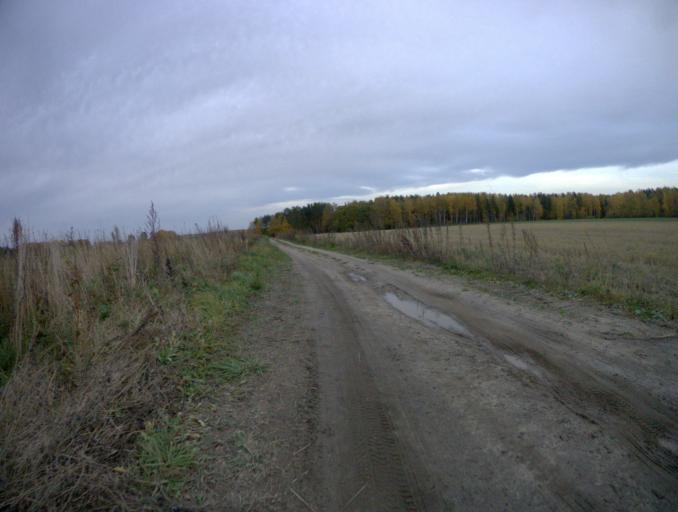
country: RU
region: Vladimir
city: Kommunar
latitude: 56.0449
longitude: 40.4748
